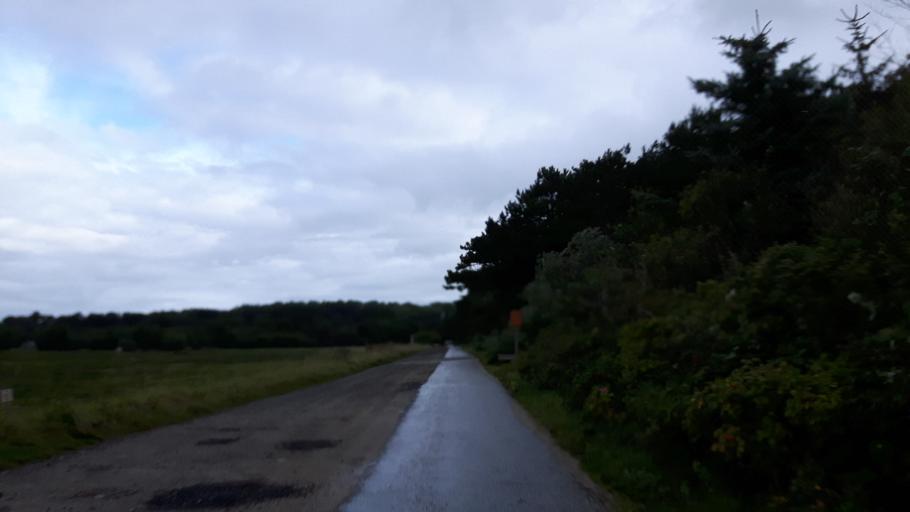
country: NL
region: Friesland
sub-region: Gemeente Ameland
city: Nes
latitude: 53.4501
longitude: 5.7572
